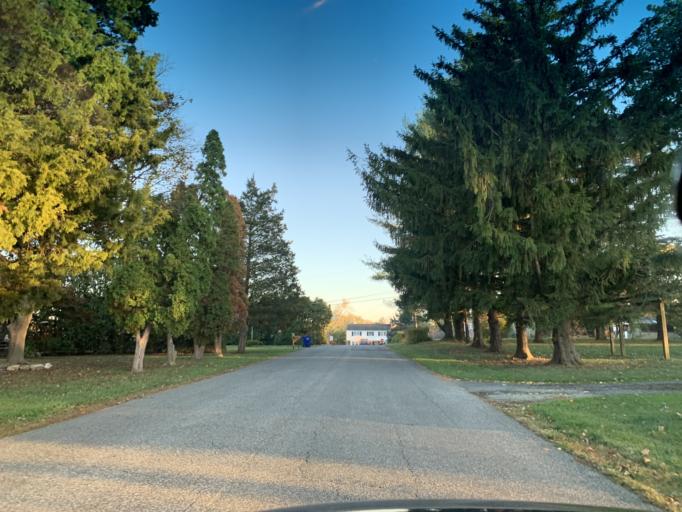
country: US
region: Maryland
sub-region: Harford County
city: Bel Air North
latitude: 39.5569
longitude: -76.3743
